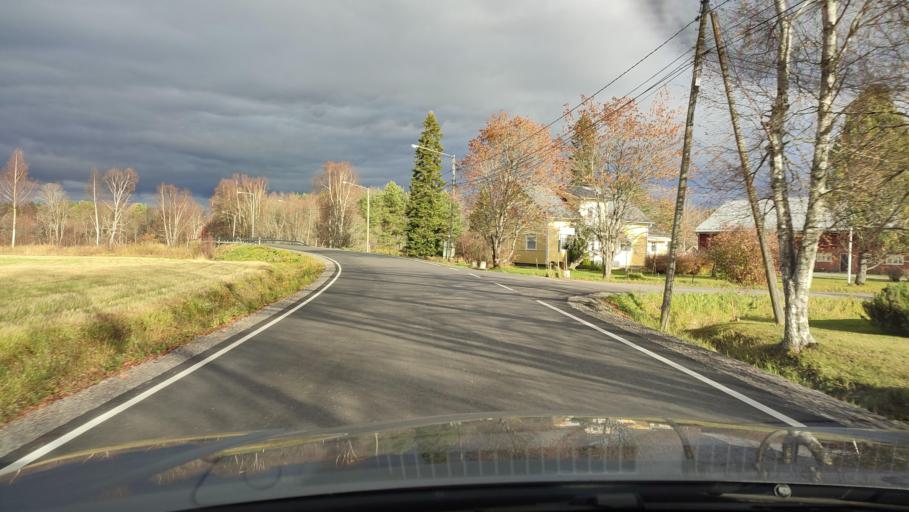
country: FI
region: Southern Ostrobothnia
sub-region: Suupohja
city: Karijoki
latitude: 62.2377
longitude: 21.5762
